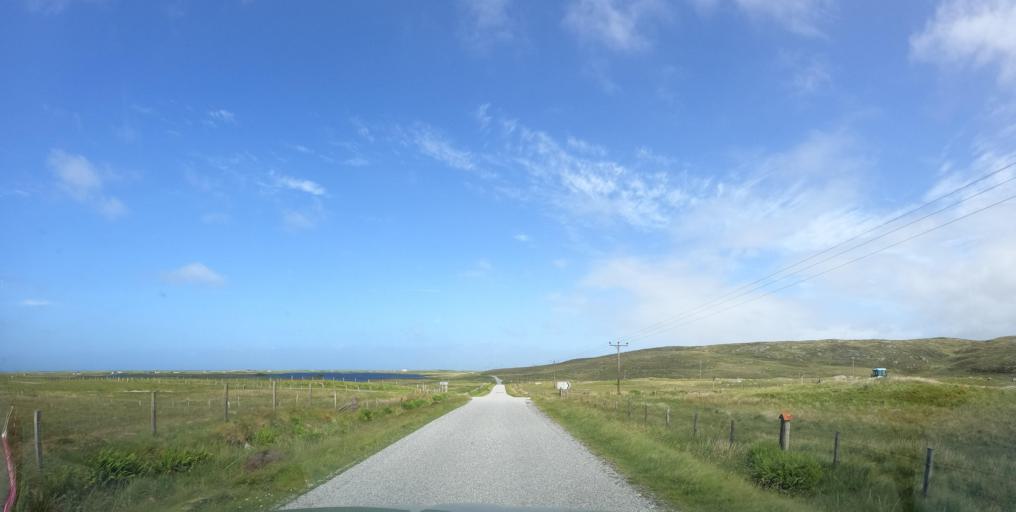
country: GB
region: Scotland
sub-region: Eilean Siar
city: Isle of South Uist
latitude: 57.1373
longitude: -7.3658
